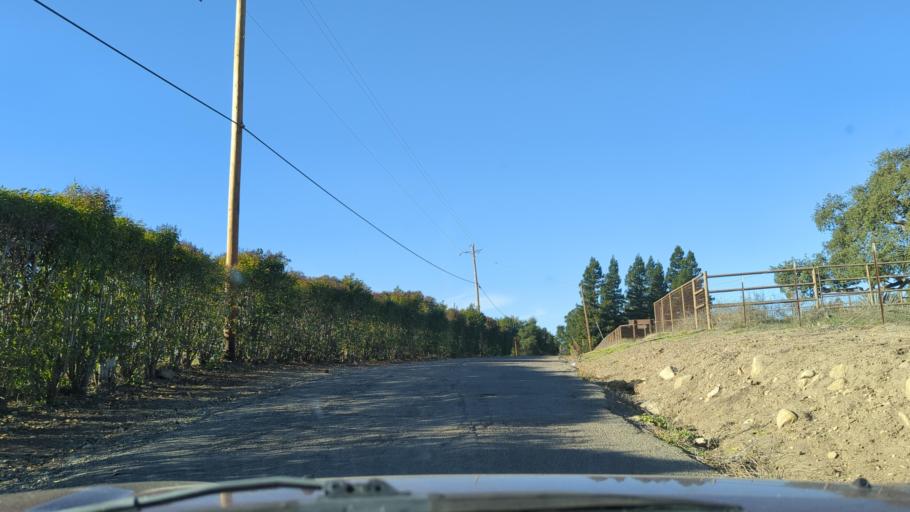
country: US
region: California
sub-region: Santa Barbara County
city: Santa Ynez
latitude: 34.5736
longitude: -120.0975
